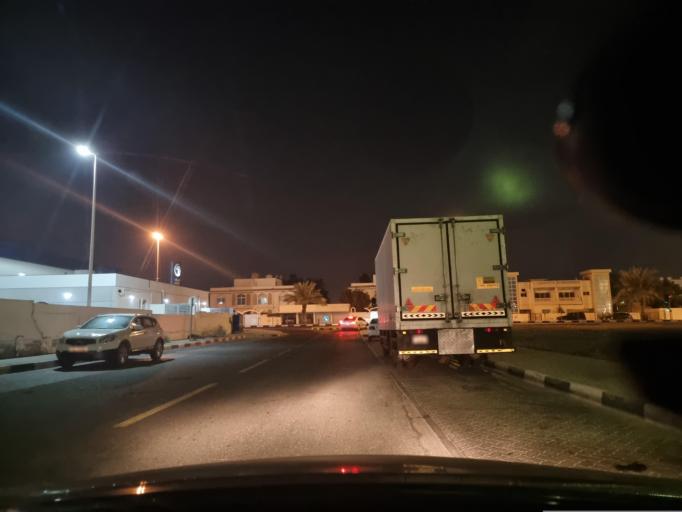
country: AE
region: Ash Shariqah
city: Sharjah
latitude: 25.3738
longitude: 55.4205
